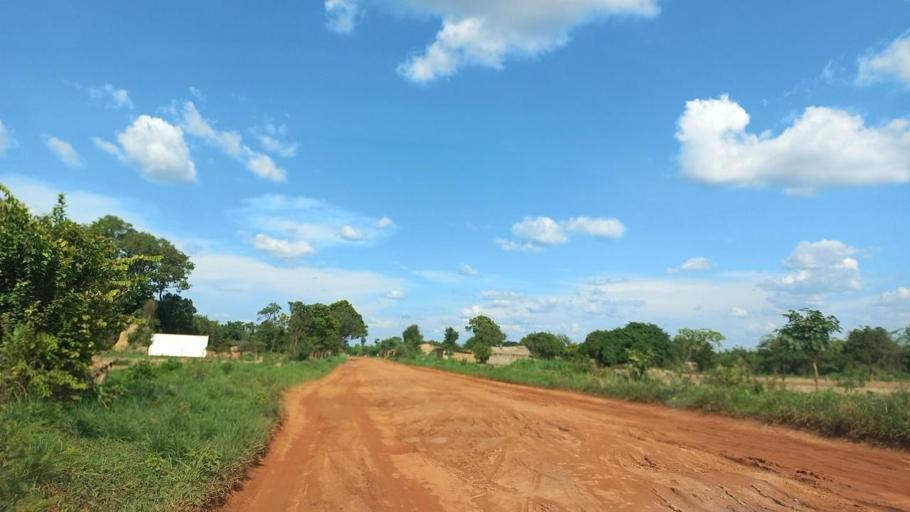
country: ZM
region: Copperbelt
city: Kitwe
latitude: -12.8662
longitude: 28.3701
